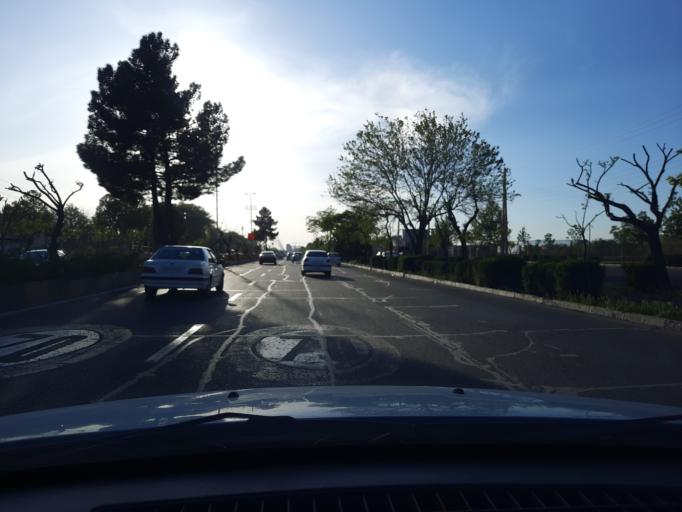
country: IR
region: Qazvin
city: Qazvin
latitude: 36.2623
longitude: 50.0437
